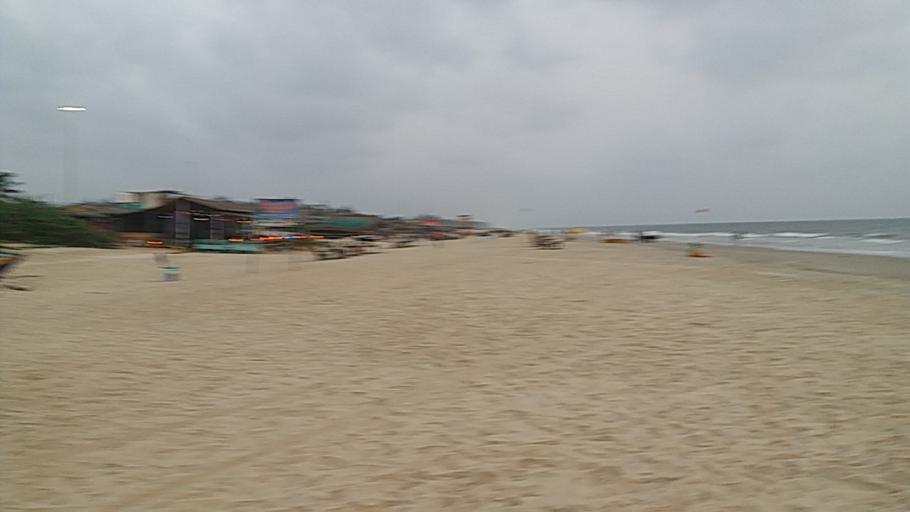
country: IN
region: Goa
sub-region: South Goa
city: Benaulim
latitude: 15.2565
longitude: 73.9190
